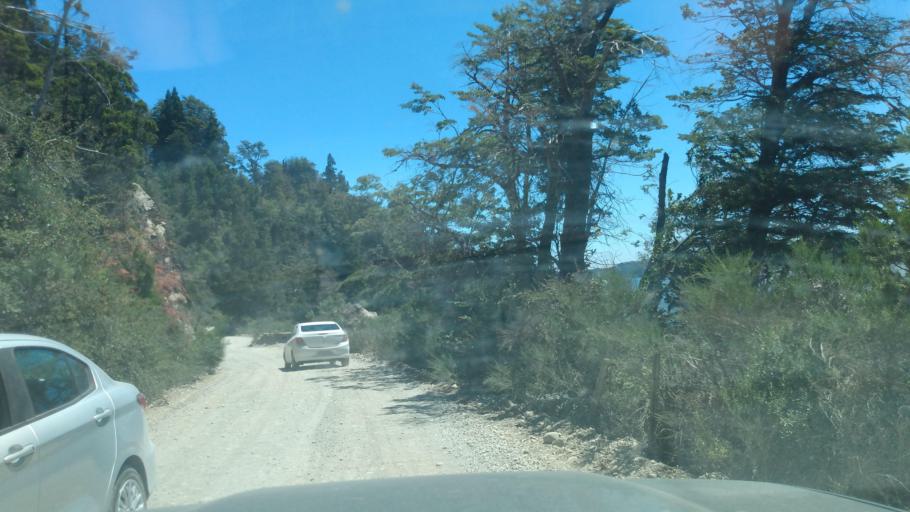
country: AR
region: Rio Negro
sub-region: Departamento de Bariloche
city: San Carlos de Bariloche
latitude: -41.1032
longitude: -71.4876
